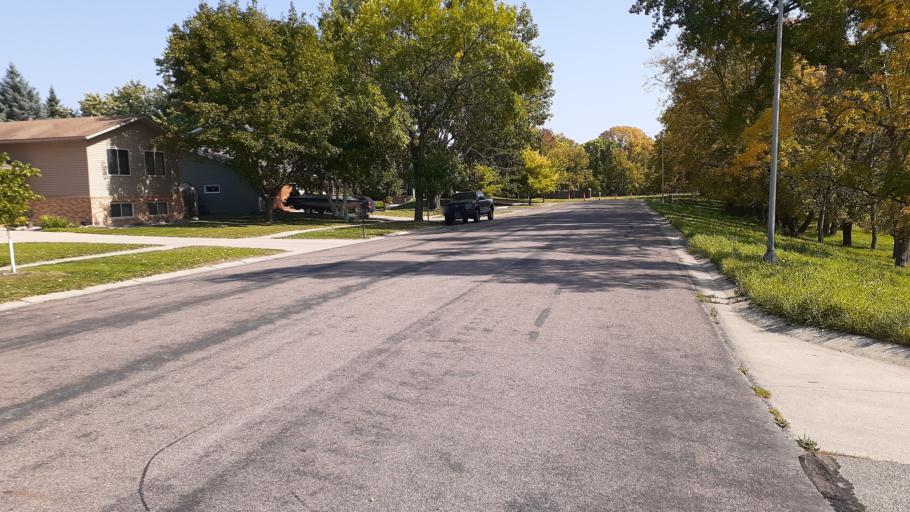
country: US
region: Minnesota
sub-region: Clay County
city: Oakport
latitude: 46.9194
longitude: -96.7653
